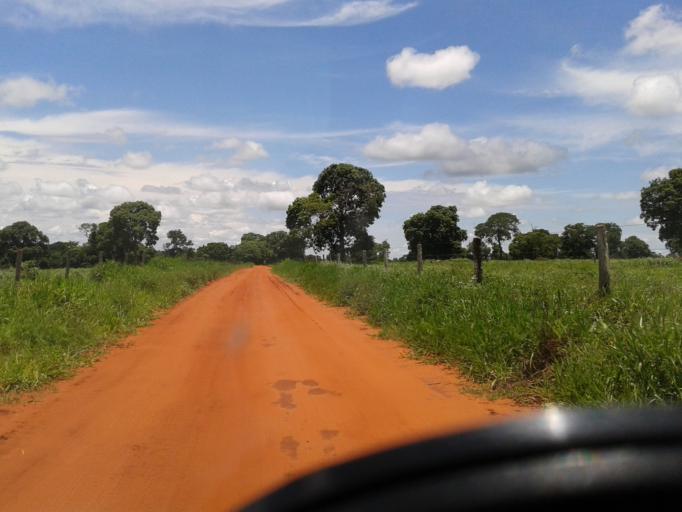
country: BR
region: Minas Gerais
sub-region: Santa Vitoria
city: Santa Vitoria
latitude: -18.9517
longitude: -49.8634
